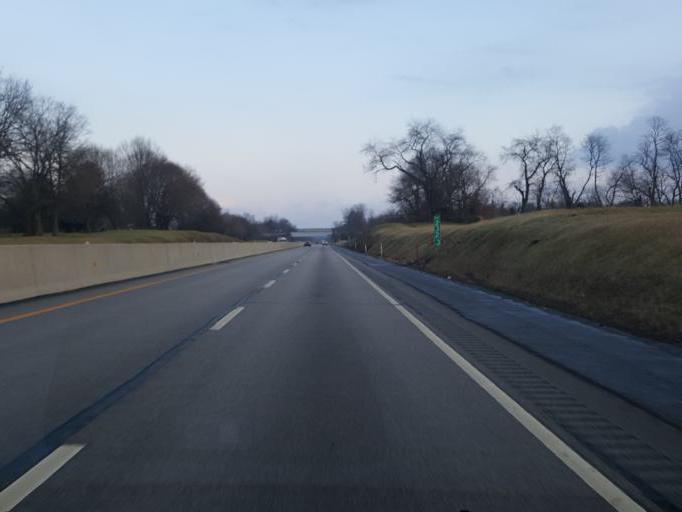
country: US
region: Pennsylvania
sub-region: Cumberland County
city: Mechanicsburg
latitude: 40.2048
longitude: -77.0488
